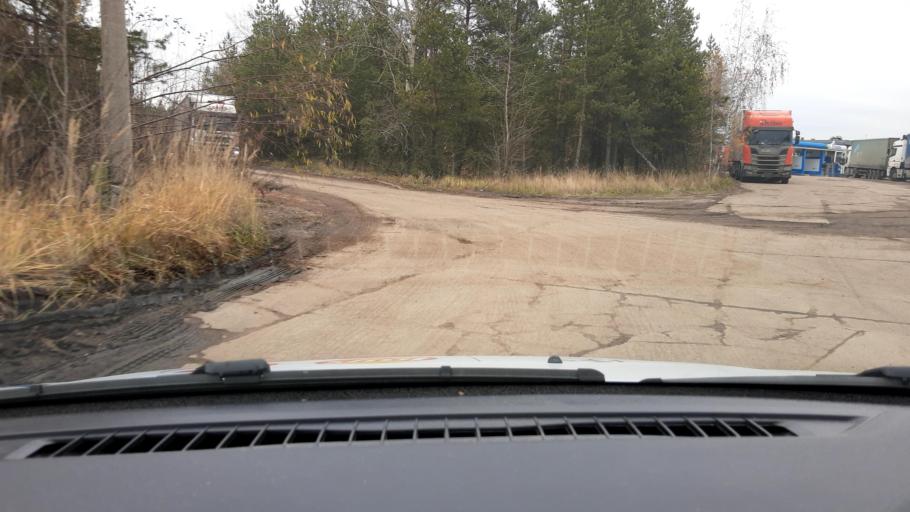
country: RU
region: Nizjnij Novgorod
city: Dzerzhinsk
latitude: 56.2771
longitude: 43.4772
